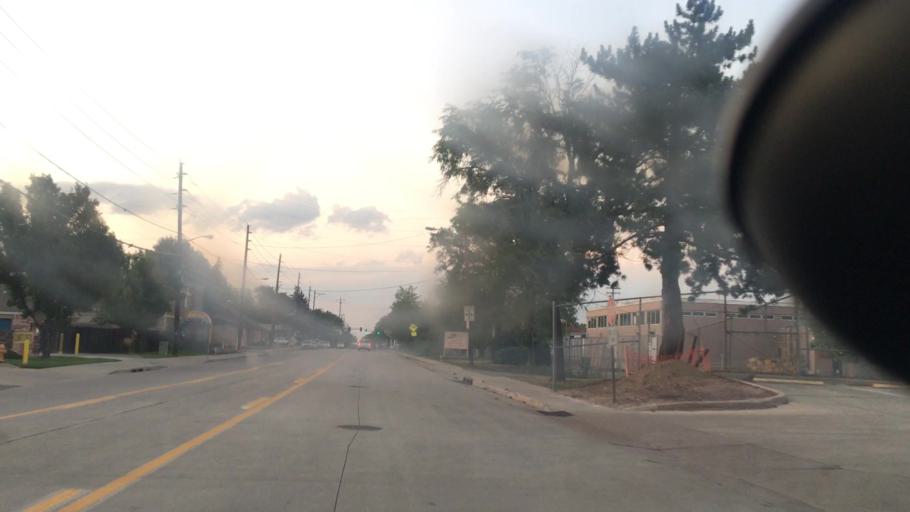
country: US
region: Colorado
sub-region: Arapahoe County
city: Glendale
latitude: 39.6794
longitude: -104.9223
